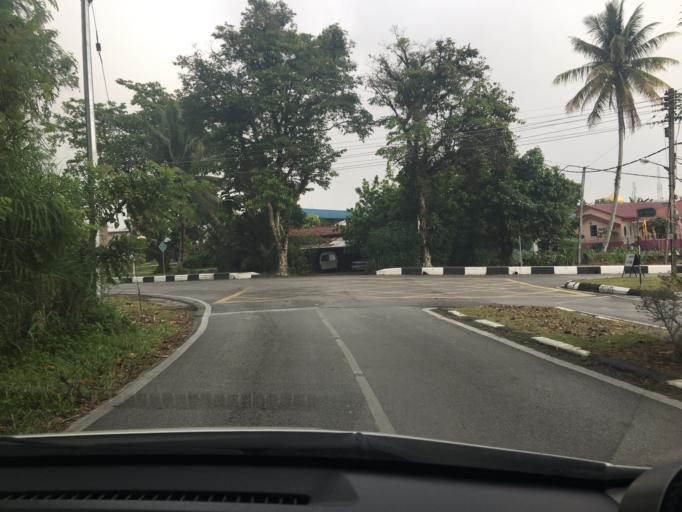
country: MY
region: Sarawak
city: Kuching
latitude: 1.4129
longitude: 110.1558
